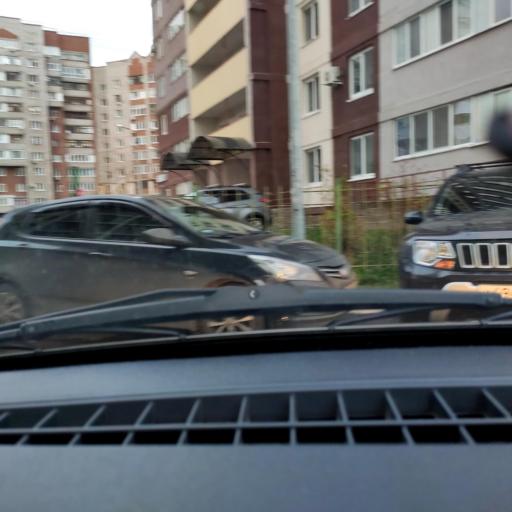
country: RU
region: Bashkortostan
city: Ufa
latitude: 54.7766
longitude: 56.1076
